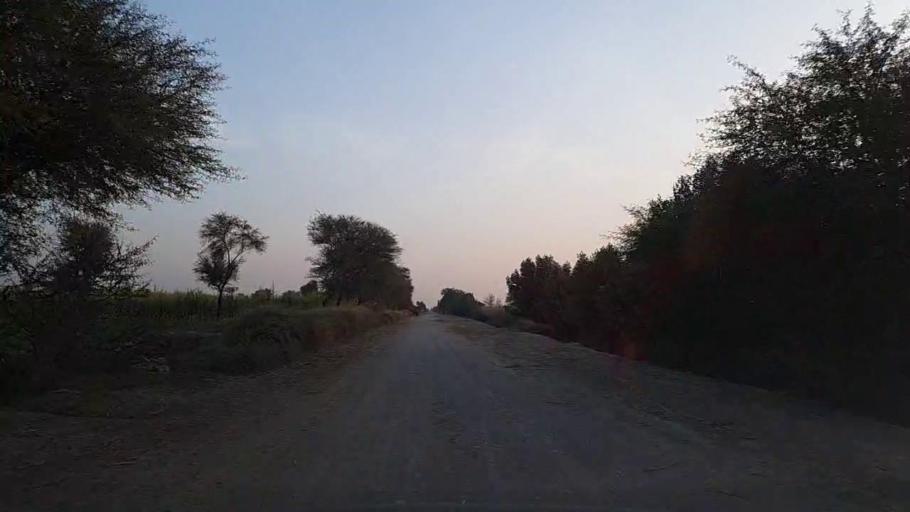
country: PK
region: Sindh
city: Tando Mittha Khan
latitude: 25.9750
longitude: 69.1105
